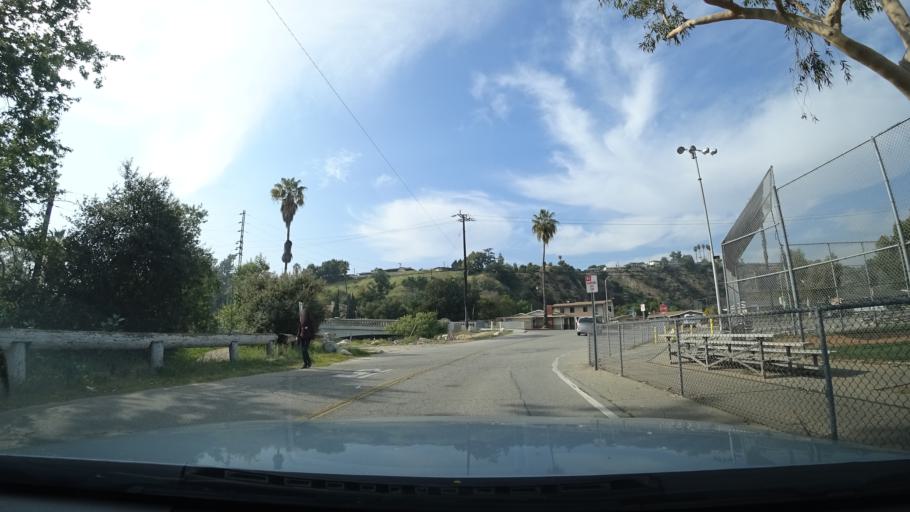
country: US
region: California
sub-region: Los Angeles County
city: South Pasadena
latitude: 34.1213
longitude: -118.1675
